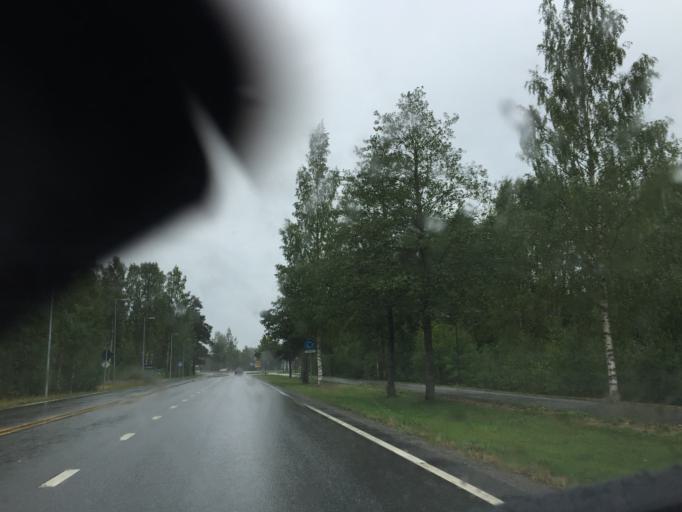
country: NO
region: Akershus
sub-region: Nannestad
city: Teigebyen
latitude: 60.1806
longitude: 11.0842
